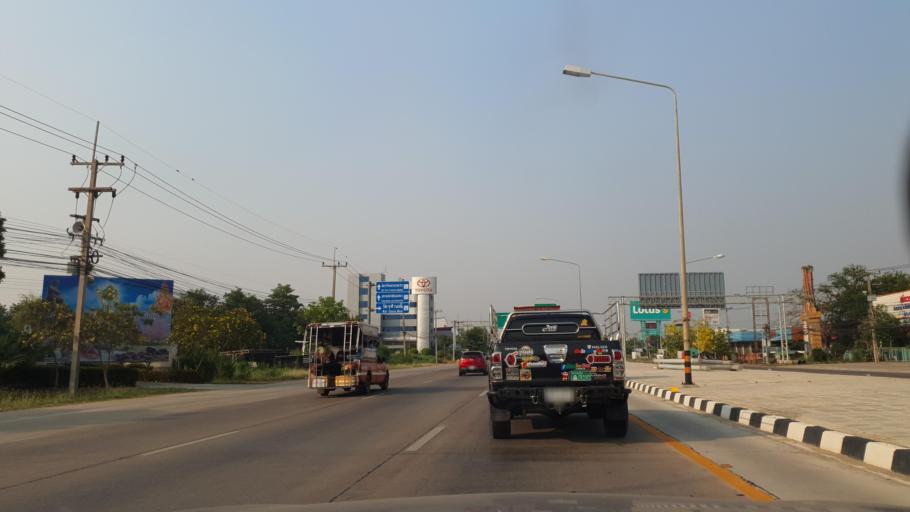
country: TH
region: Phitsanulok
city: Phitsanulok
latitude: 16.7970
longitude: 100.2124
